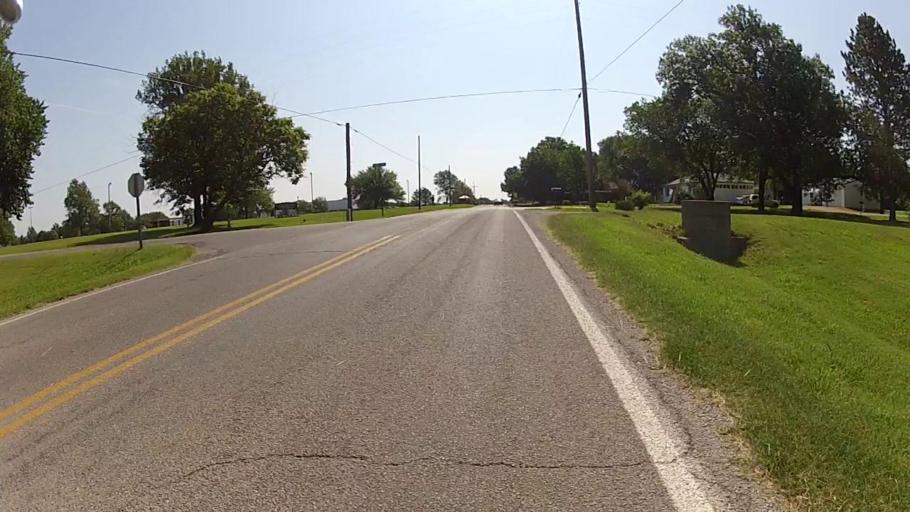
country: US
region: Kansas
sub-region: Montgomery County
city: Independence
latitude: 37.1929
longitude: -95.7234
